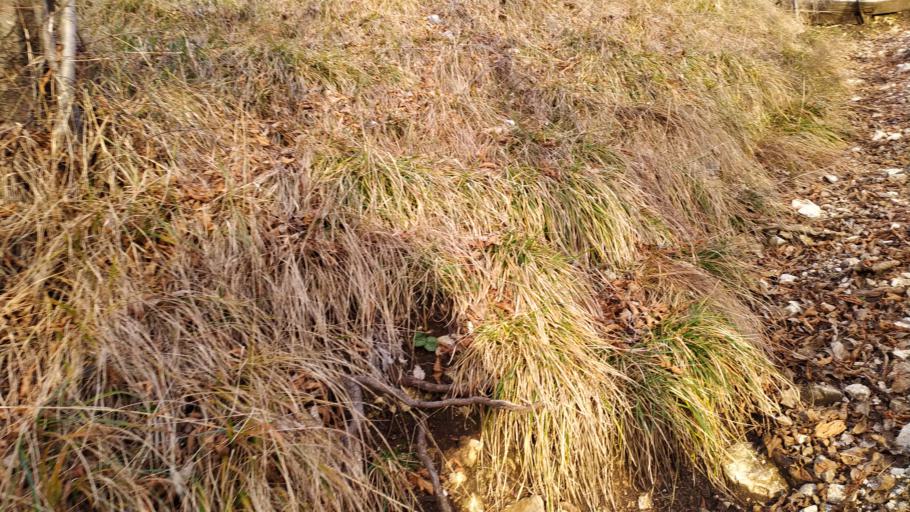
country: IT
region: Veneto
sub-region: Provincia di Vicenza
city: Velo d'Astico
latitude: 45.7674
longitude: 11.3703
